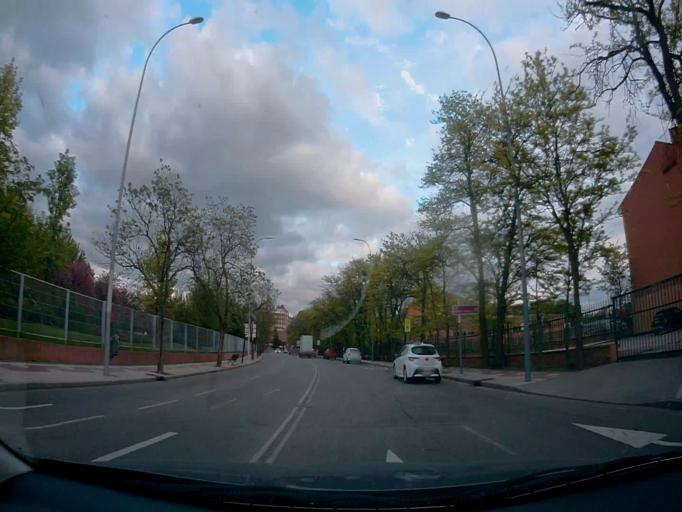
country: ES
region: Madrid
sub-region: Provincia de Madrid
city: Alcorcon
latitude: 40.3407
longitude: -3.8402
